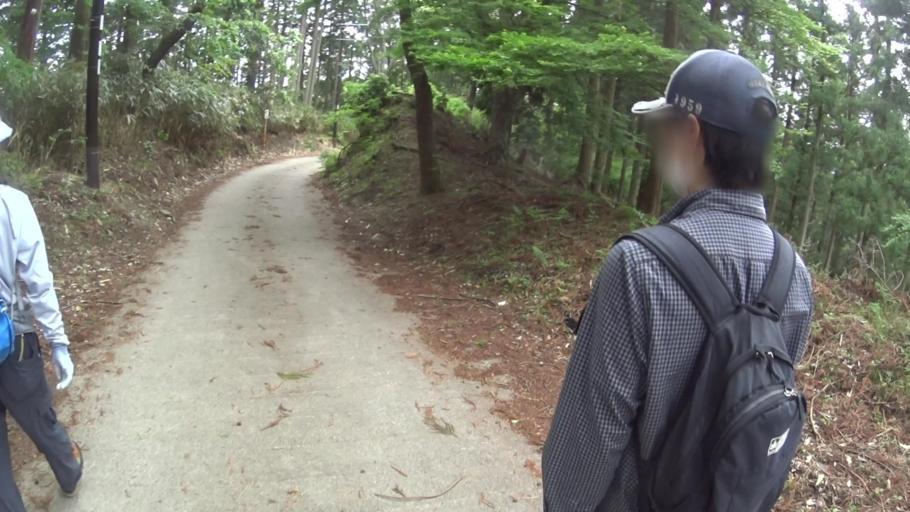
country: JP
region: Nara
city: Yoshino-cho
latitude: 34.3469
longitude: 135.8792
